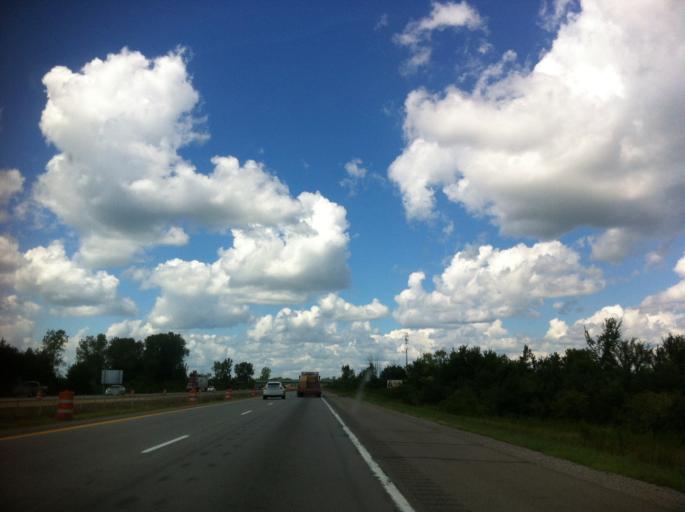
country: US
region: Michigan
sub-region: Washtenaw County
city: Milan
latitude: 42.1080
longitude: -83.6821
